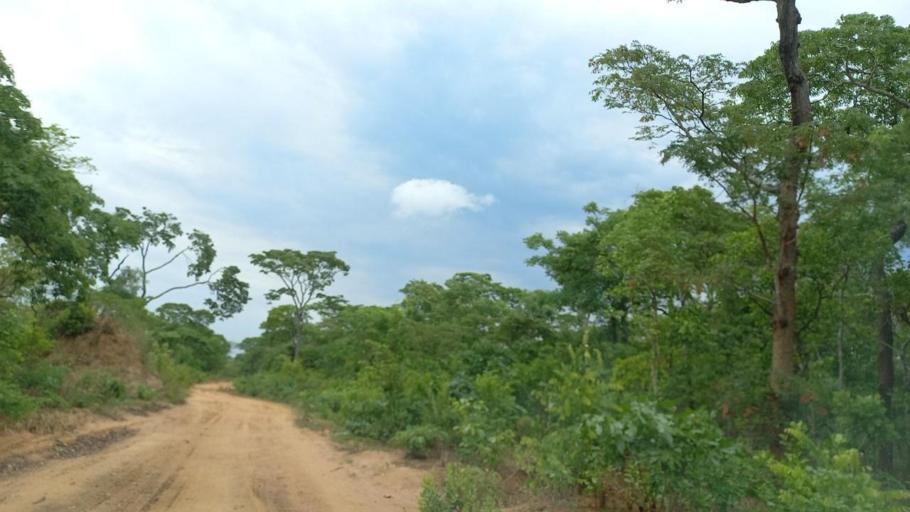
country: ZM
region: North-Western
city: Kalengwa
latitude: -13.5390
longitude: 24.9784
